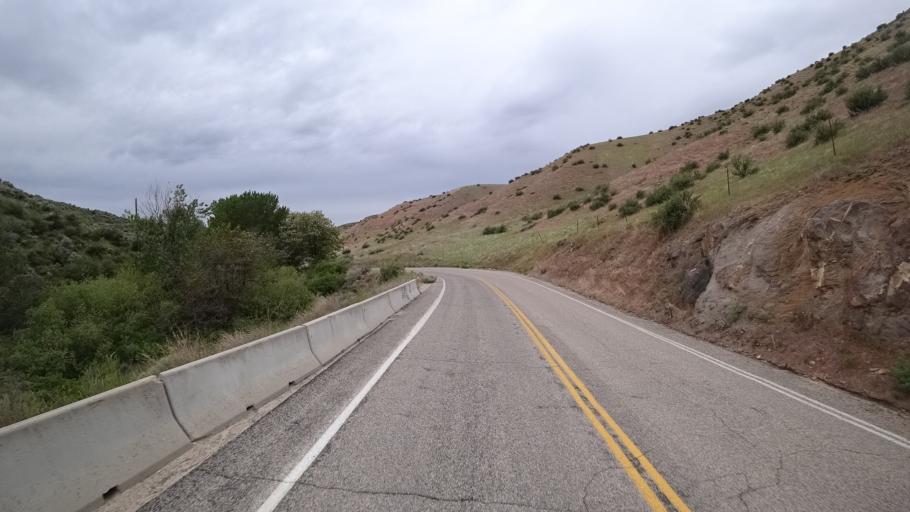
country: US
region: Idaho
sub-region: Ada County
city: Boise
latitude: 43.6165
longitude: -116.1463
